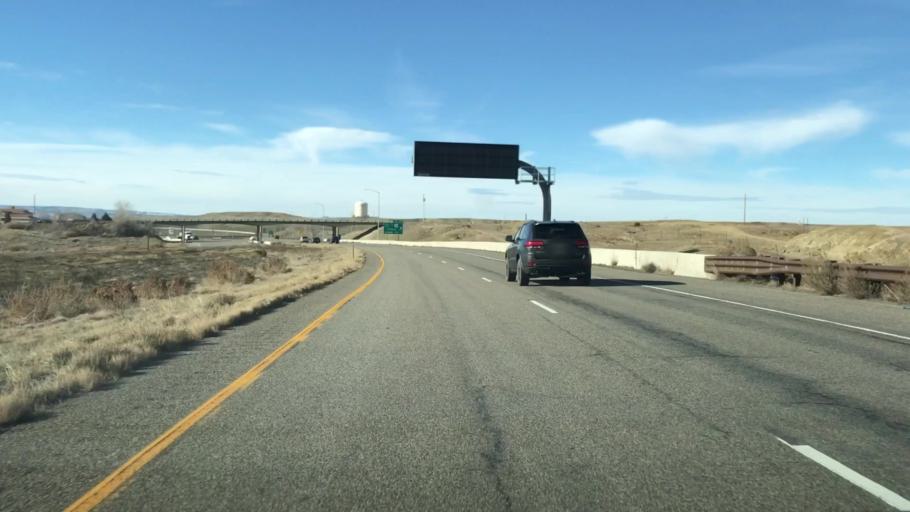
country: US
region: Colorado
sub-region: Mesa County
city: Clifton
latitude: 39.1075
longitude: -108.4381
